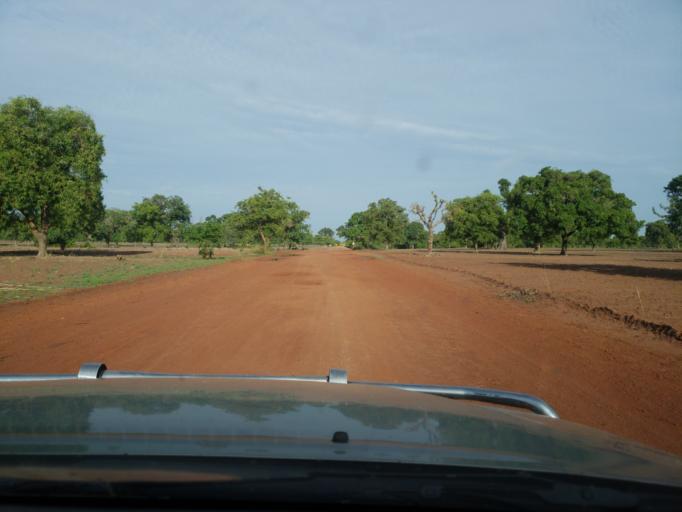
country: ML
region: Sikasso
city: Koutiala
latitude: 12.4192
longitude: -5.7018
